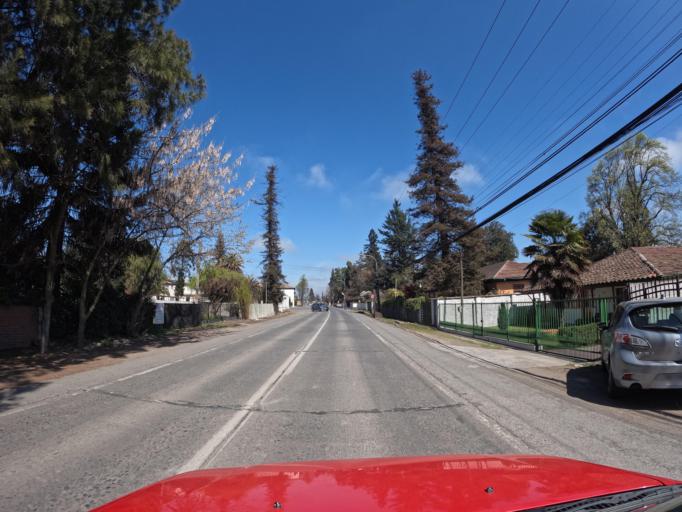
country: CL
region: Maule
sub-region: Provincia de Curico
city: Molina
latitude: -35.0767
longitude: -71.2593
